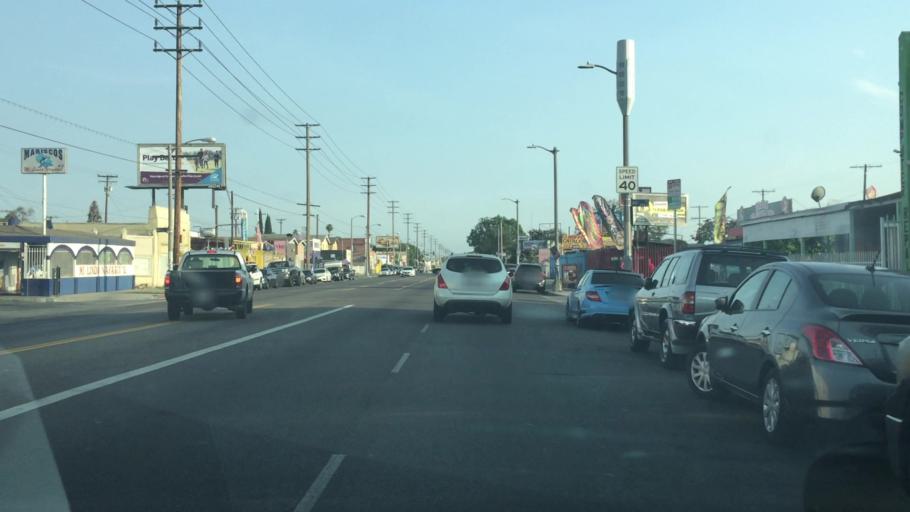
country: US
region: California
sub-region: Los Angeles County
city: Florence-Graham
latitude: 33.9669
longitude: -118.2565
